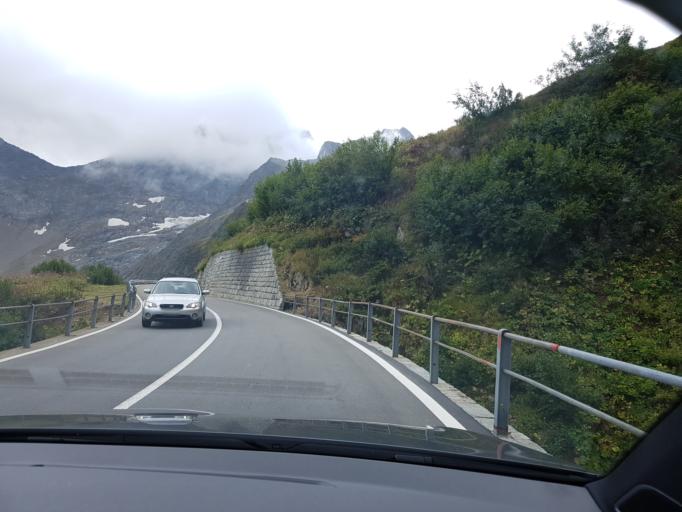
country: CH
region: Obwalden
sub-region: Obwalden
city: Engelberg
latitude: 46.7371
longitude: 8.4550
